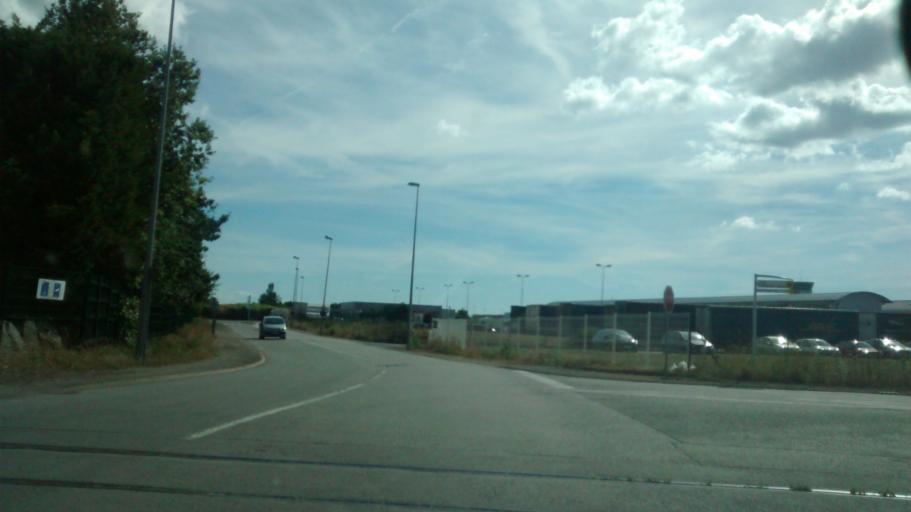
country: FR
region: Pays de la Loire
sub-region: Departement de la Loire-Atlantique
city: Bouguenais
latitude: 47.1539
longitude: -1.5990
